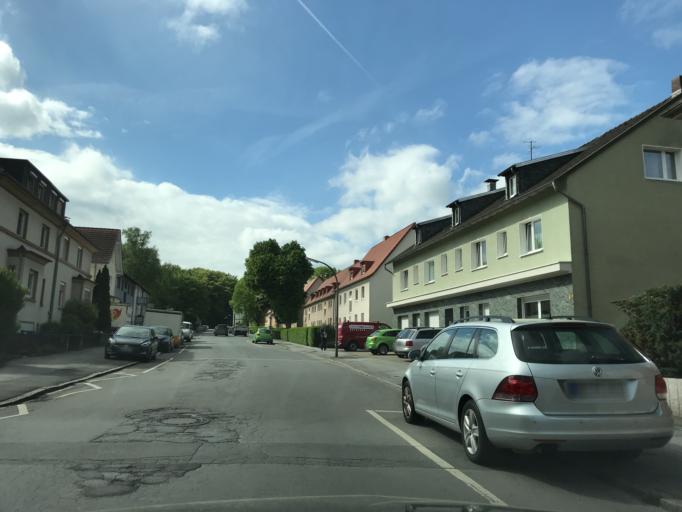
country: DE
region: North Rhine-Westphalia
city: Witten
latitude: 51.4869
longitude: 7.3693
